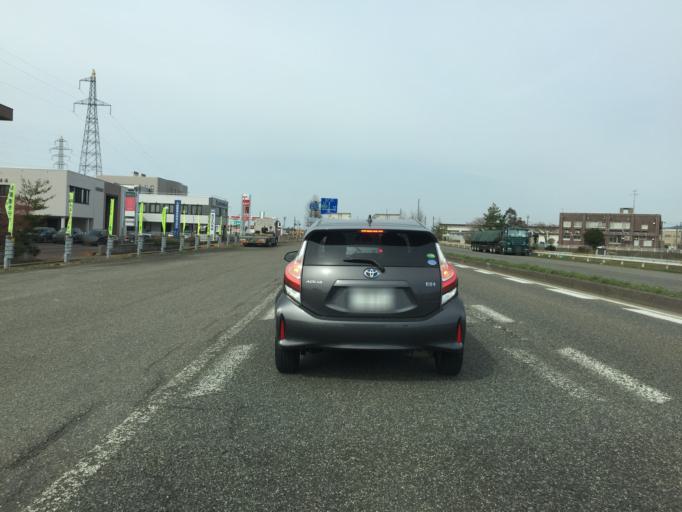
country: JP
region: Niigata
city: Nagaoka
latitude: 37.4494
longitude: 138.8743
